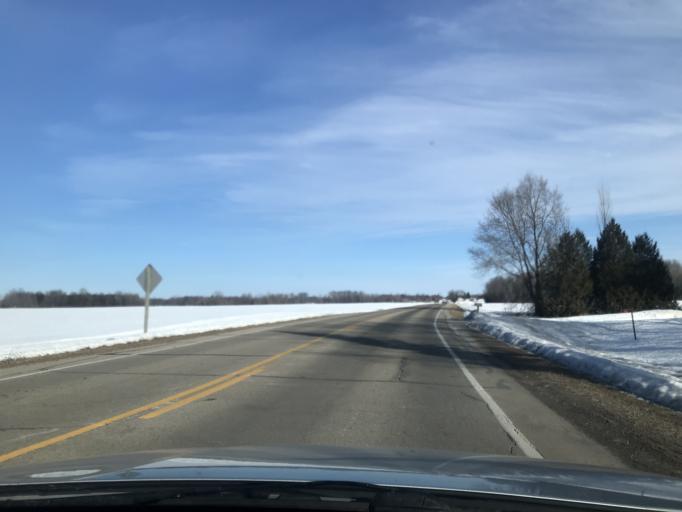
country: US
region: Wisconsin
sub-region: Oconto County
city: Oconto Falls
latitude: 44.8876
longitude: -88.1564
